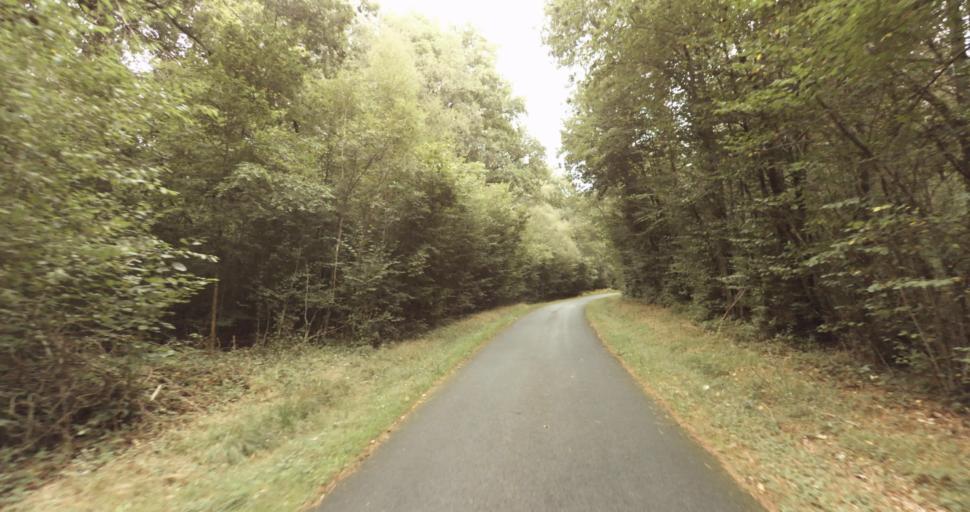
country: FR
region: Lower Normandy
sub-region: Departement de l'Orne
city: Gace
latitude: 48.8430
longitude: 0.3303
